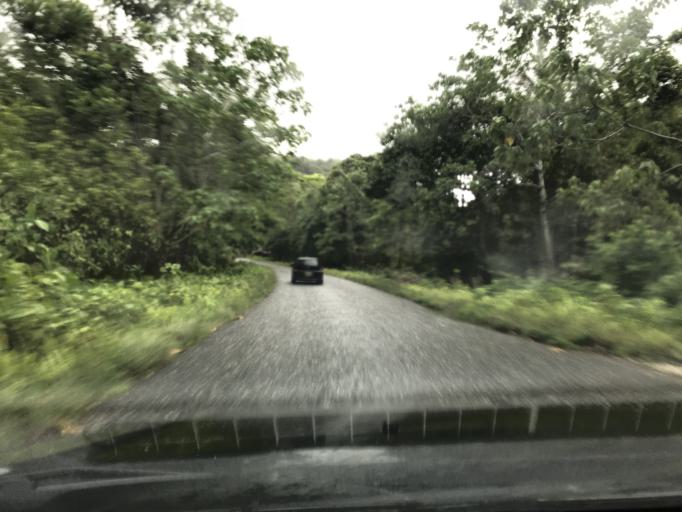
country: SB
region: Western Province
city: Gizo
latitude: -8.3123
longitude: 157.2542
